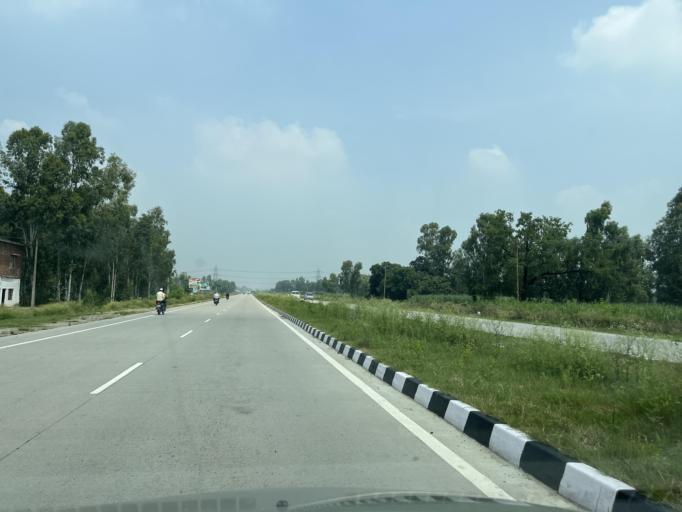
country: IN
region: Uttar Pradesh
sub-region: Bijnor
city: Najibabad
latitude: 29.5541
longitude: 78.3391
